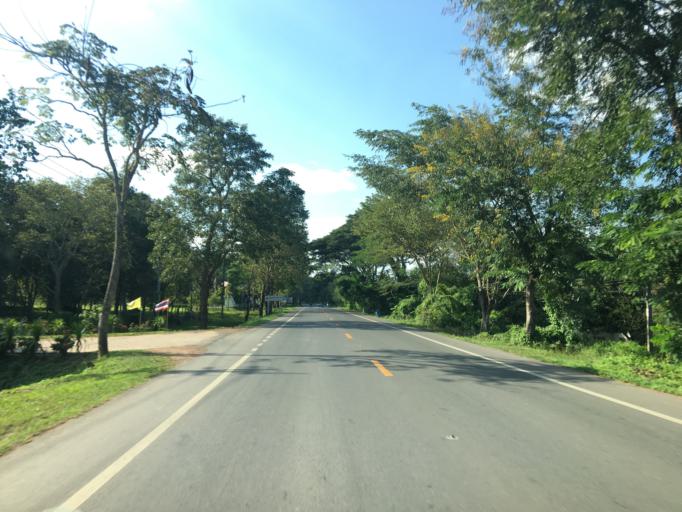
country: TH
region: Phayao
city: Chun
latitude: 19.3468
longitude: 100.1151
